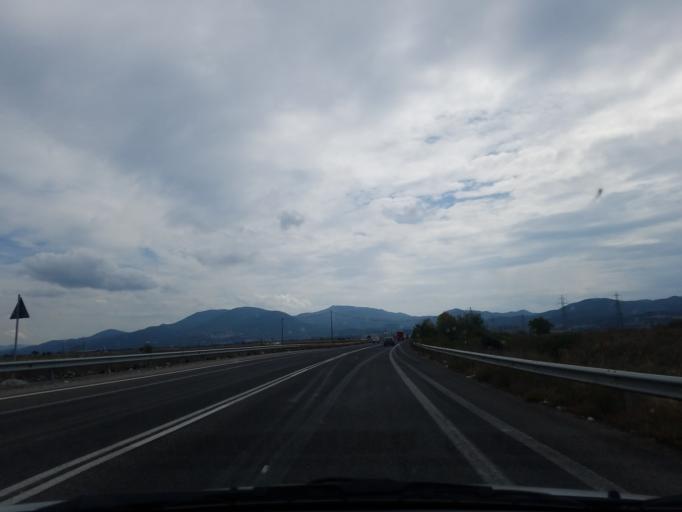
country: GR
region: Central Greece
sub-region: Nomos Fthiotidos
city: Domokos
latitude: 39.0538
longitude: 22.3399
